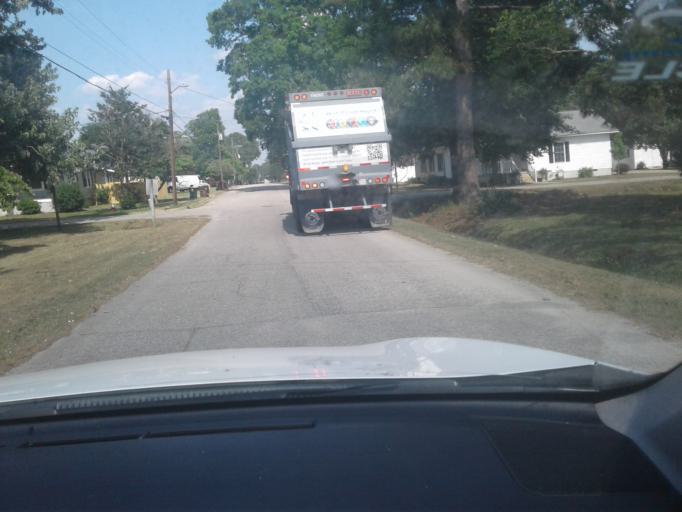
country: US
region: North Carolina
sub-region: Harnett County
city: Erwin
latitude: 35.3239
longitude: -78.6813
